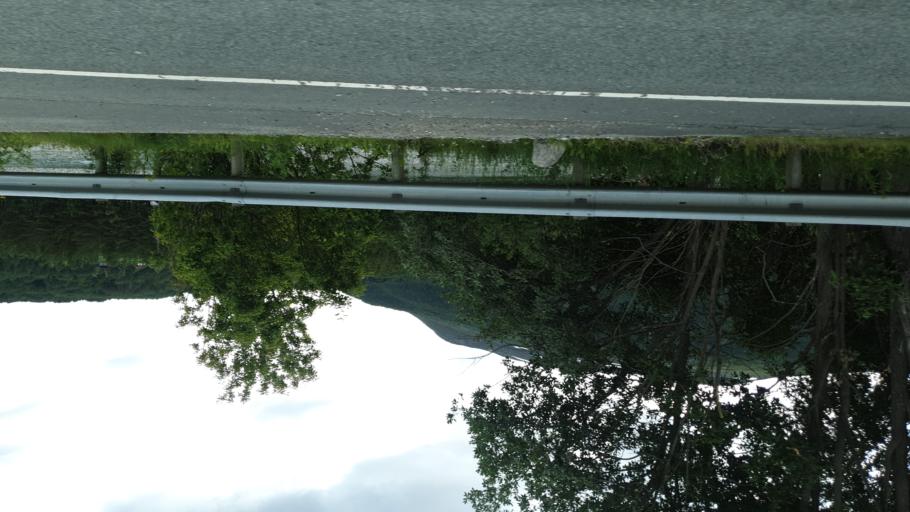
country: NO
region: Sor-Trondelag
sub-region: Oppdal
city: Oppdal
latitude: 62.5534
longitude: 9.6328
